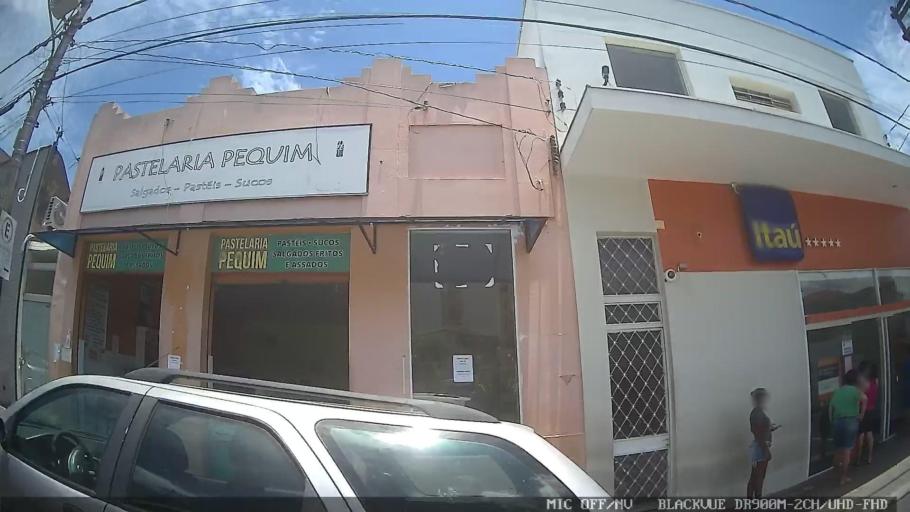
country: BR
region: Sao Paulo
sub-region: Laranjal Paulista
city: Laranjal Paulista
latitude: -23.0500
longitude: -47.8374
